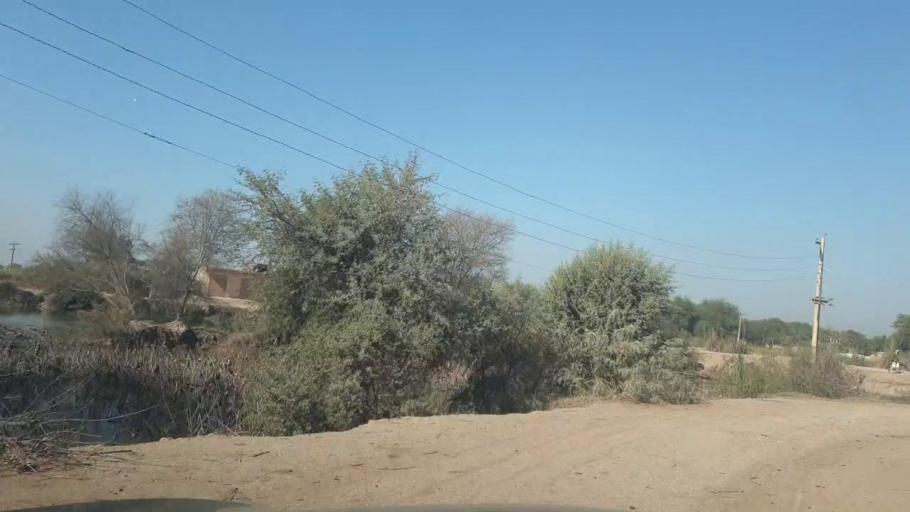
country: PK
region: Sindh
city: Mirpur Mathelo
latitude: 28.1436
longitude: 69.5325
